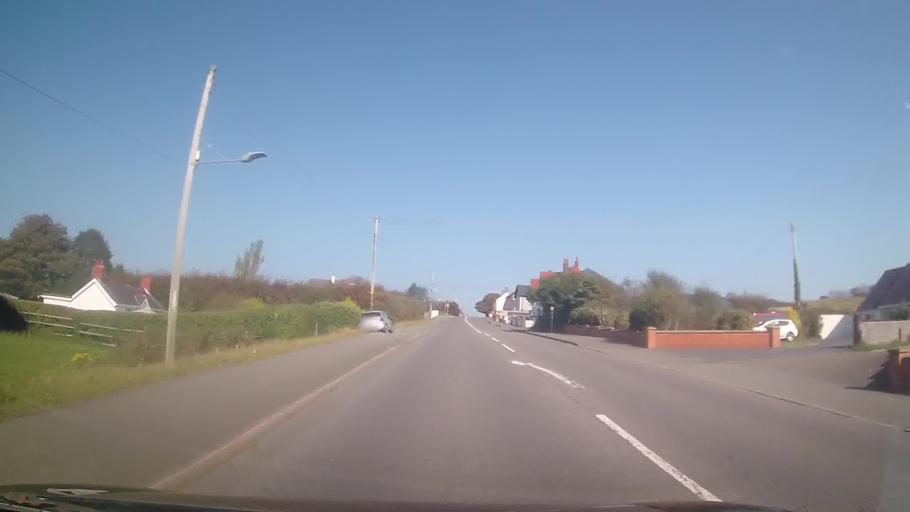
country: GB
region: Wales
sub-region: County of Ceredigion
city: Cardigan
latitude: 52.0992
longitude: -4.6164
